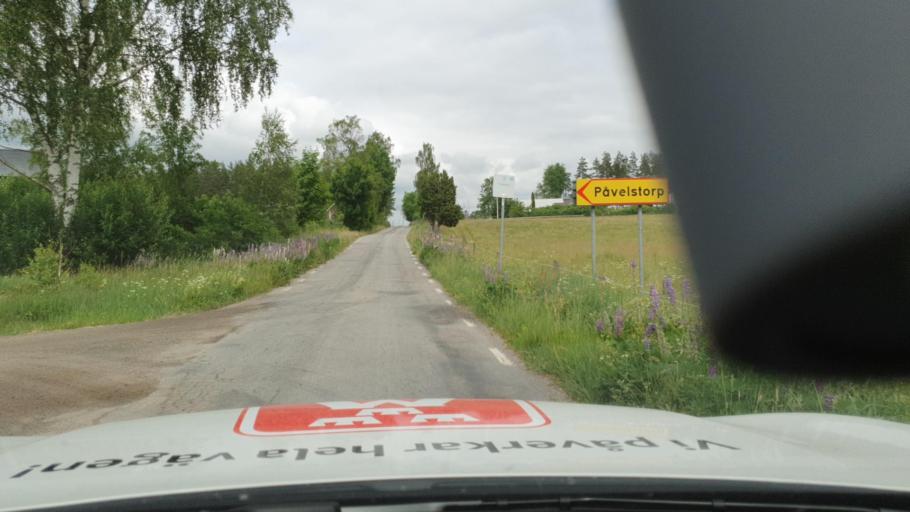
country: SE
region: Vaestra Goetaland
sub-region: Tidaholms Kommun
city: Tidaholm
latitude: 58.1485
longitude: 14.0265
